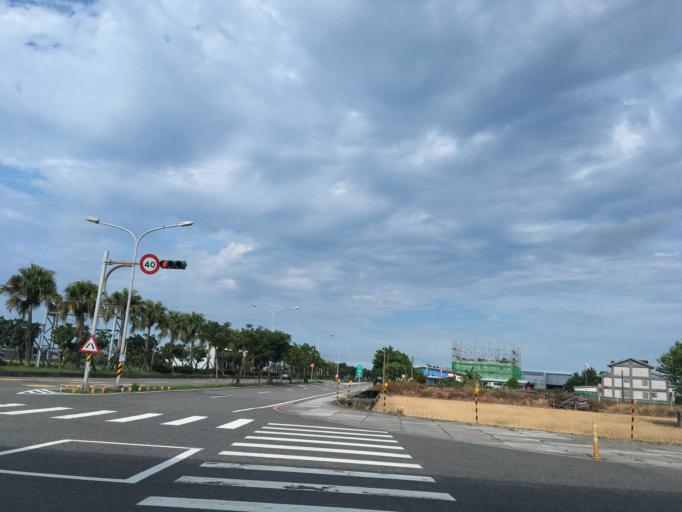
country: TW
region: Taiwan
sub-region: Yilan
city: Yilan
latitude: 24.6798
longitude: 121.7937
